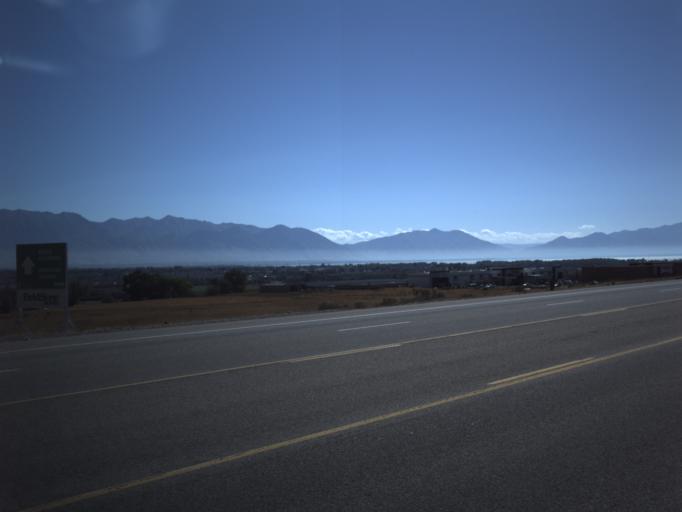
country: US
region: Utah
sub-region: Utah County
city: Saratoga Springs
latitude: 40.4050
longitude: -111.9209
